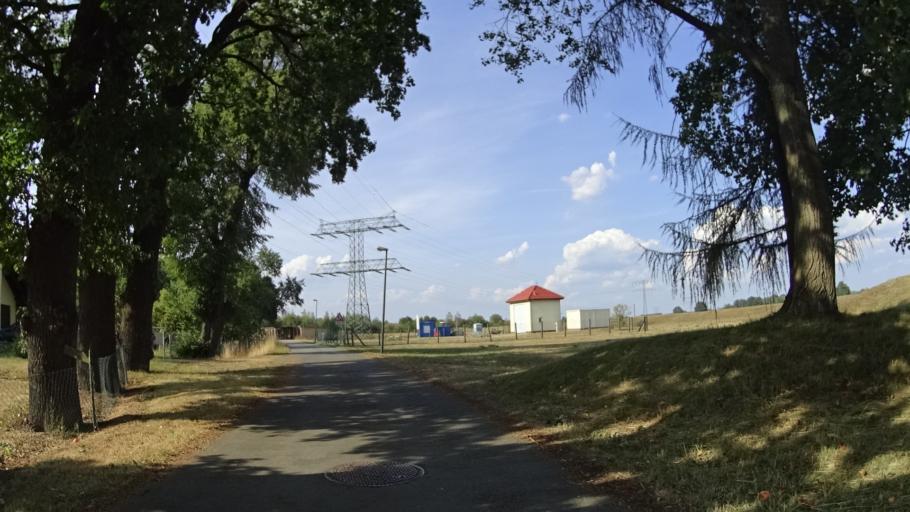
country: DE
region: Saxony
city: Ostritz
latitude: 51.0722
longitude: 14.9678
